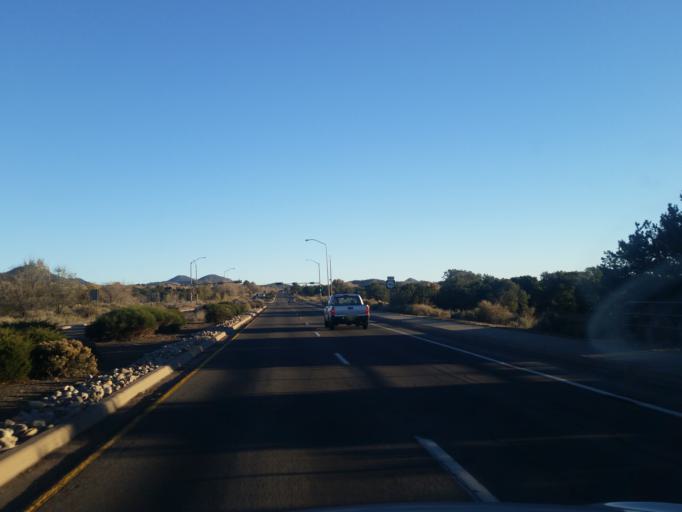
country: US
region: New Mexico
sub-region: Santa Fe County
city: Santa Fe
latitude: 35.6529
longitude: -105.9374
